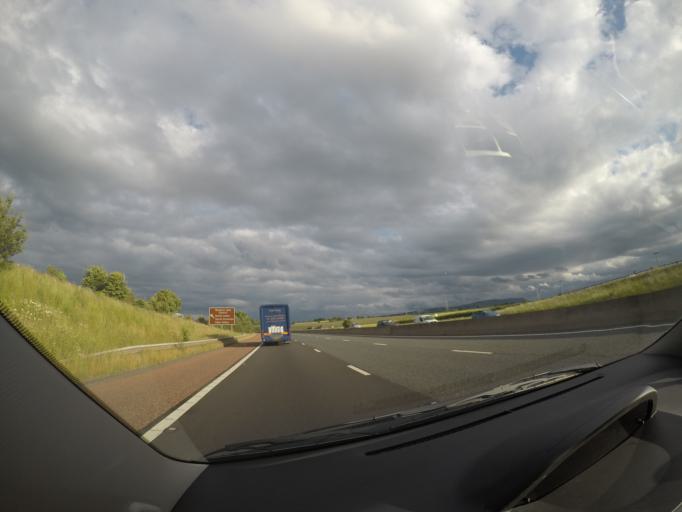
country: GB
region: England
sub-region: Cumbria
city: Penrith
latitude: 54.6620
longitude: -2.7716
